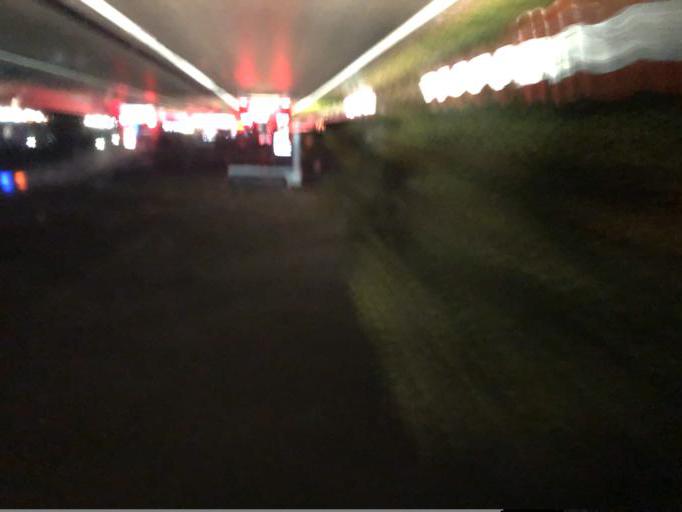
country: GB
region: England
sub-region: Staffordshire
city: Stone
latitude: 52.8714
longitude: -2.1654
